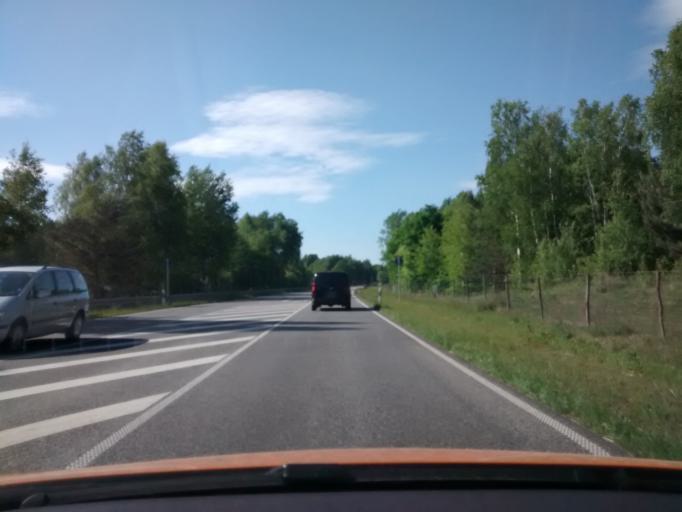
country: DE
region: Brandenburg
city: Luckenwalde
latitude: 52.0885
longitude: 13.1229
